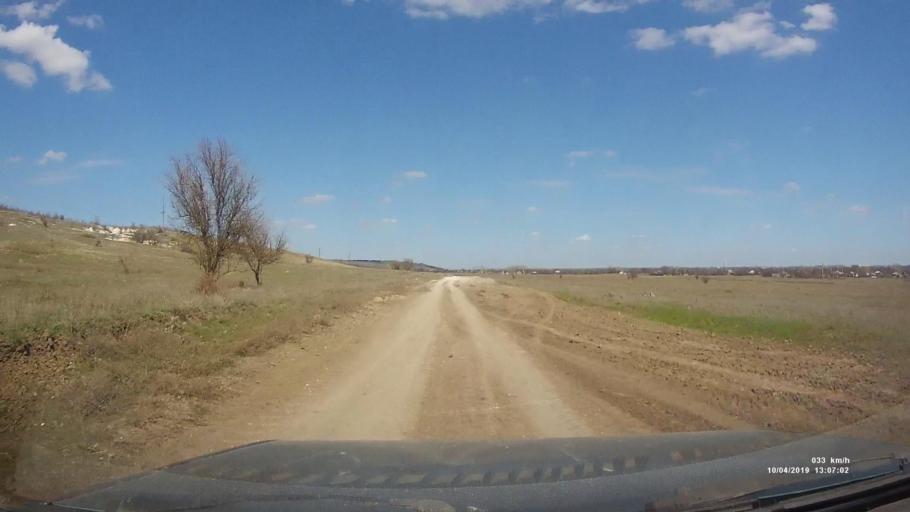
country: RU
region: Rostov
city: Masalovka
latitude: 48.3934
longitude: 40.2383
